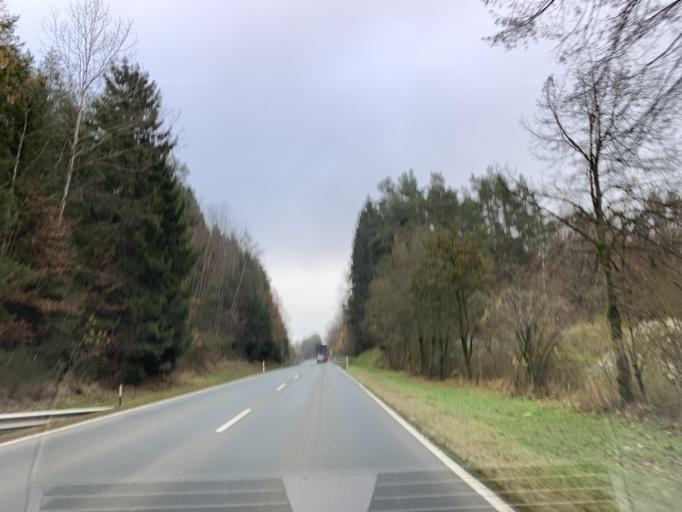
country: DE
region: Bavaria
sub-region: Upper Palatinate
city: Roetz
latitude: 49.3469
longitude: 12.4968
